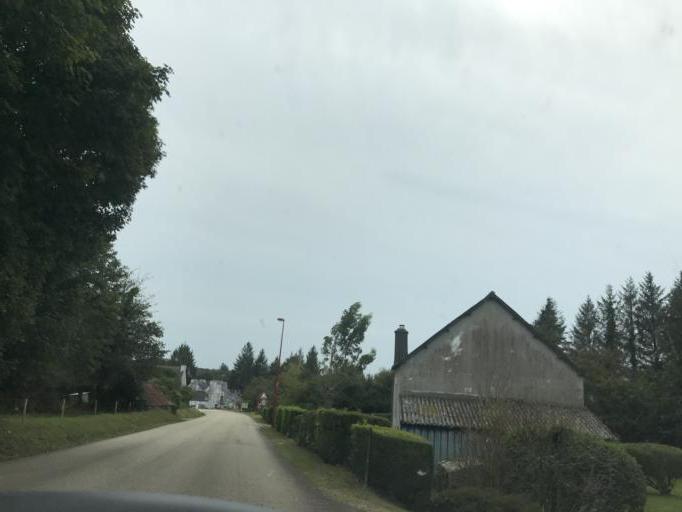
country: FR
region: Brittany
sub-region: Departement du Finistere
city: Plouneour-Menez
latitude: 48.3646
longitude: -3.8506
